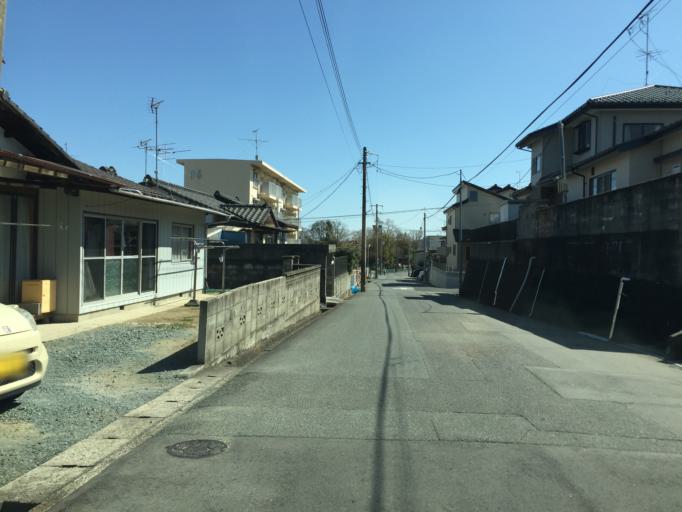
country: JP
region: Fukushima
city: Iwaki
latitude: 37.0486
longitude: 140.8548
